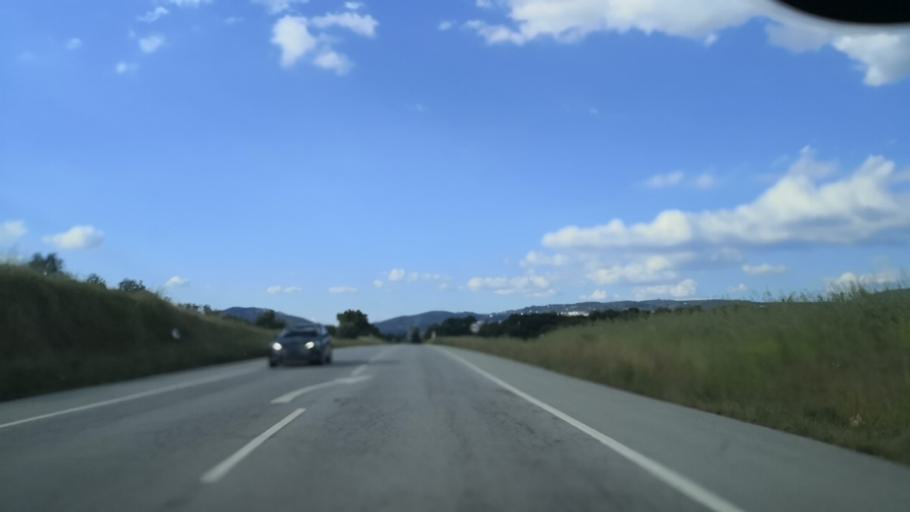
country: PT
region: Portalegre
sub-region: Portalegre
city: Portalegre
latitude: 39.2513
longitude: -7.4482
